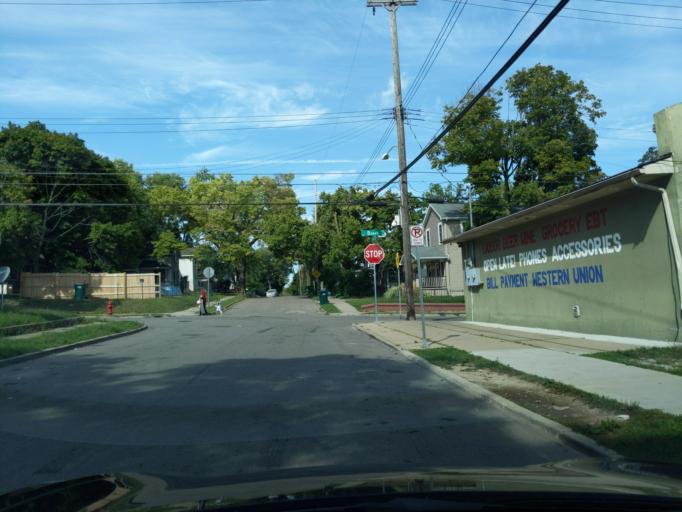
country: US
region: Michigan
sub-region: Ingham County
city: Lansing
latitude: 42.7162
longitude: -84.5419
